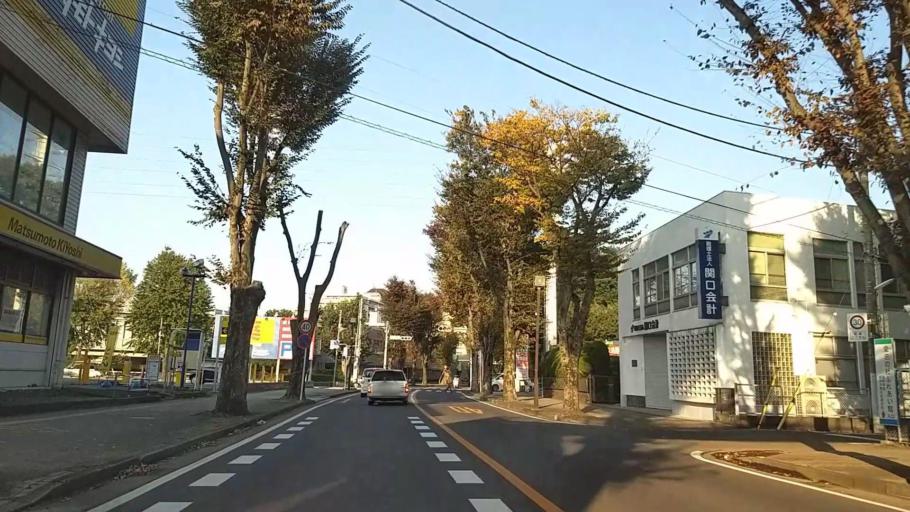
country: JP
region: Saitama
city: Tokorozawa
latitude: 35.8032
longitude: 139.4506
